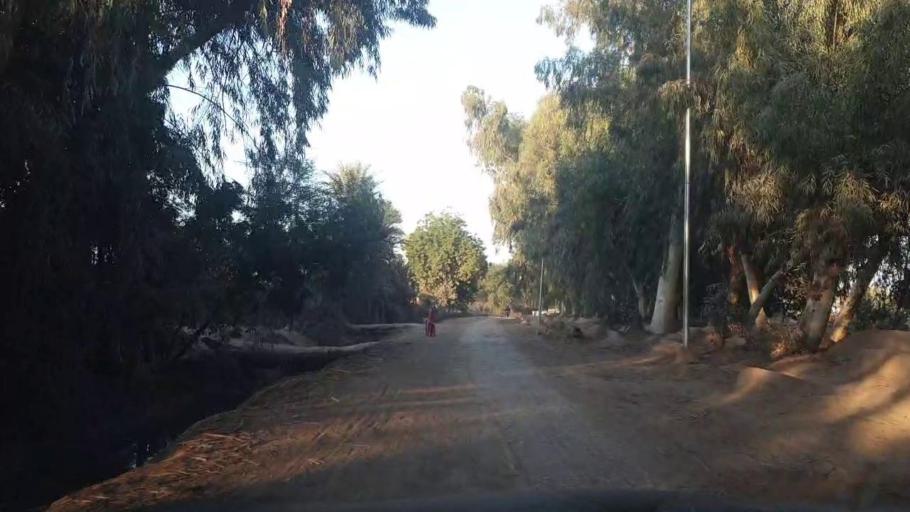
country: PK
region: Sindh
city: Ubauro
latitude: 28.1699
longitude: 69.6027
